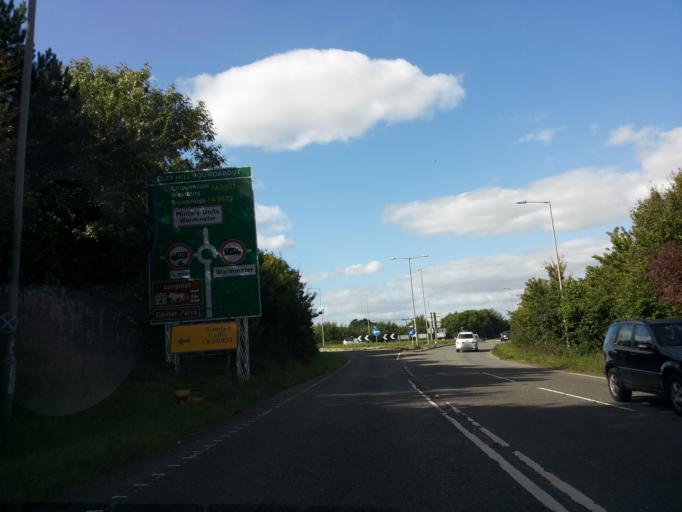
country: GB
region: England
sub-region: Wiltshire
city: Warminster
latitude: 51.1989
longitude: -2.2152
